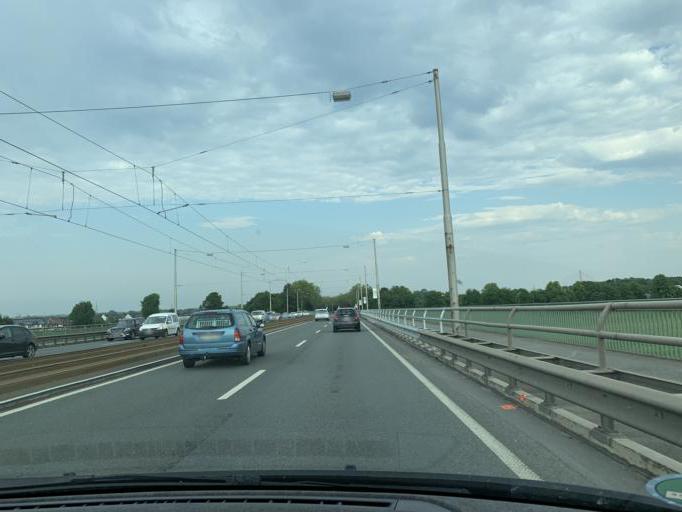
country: DE
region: North Rhine-Westphalia
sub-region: Regierungsbezirk Dusseldorf
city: Neuss
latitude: 51.1986
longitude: 6.7329
